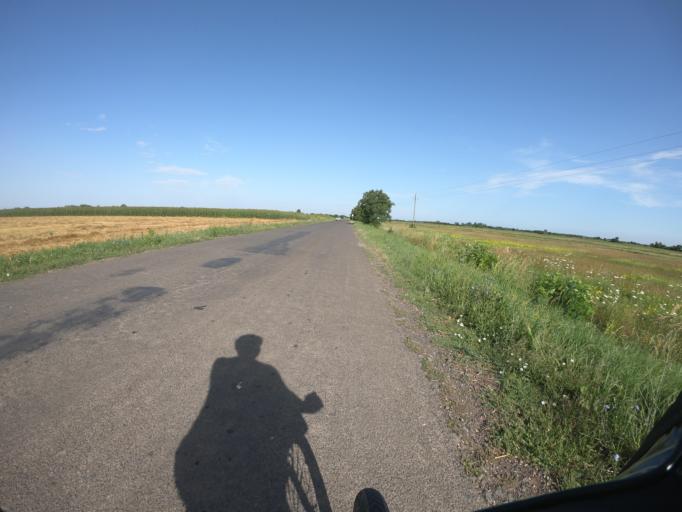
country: HU
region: Hajdu-Bihar
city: Egyek
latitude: 47.6061
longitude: 20.9857
